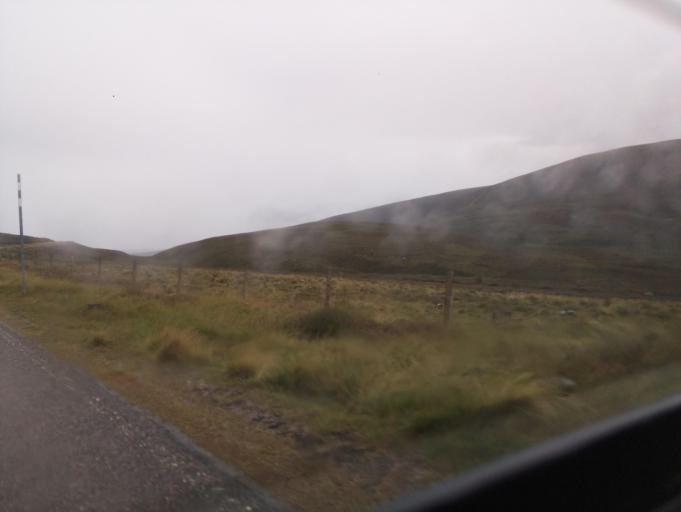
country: GB
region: Scotland
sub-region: Aberdeenshire
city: Ballater
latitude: 57.1375
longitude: -3.1576
